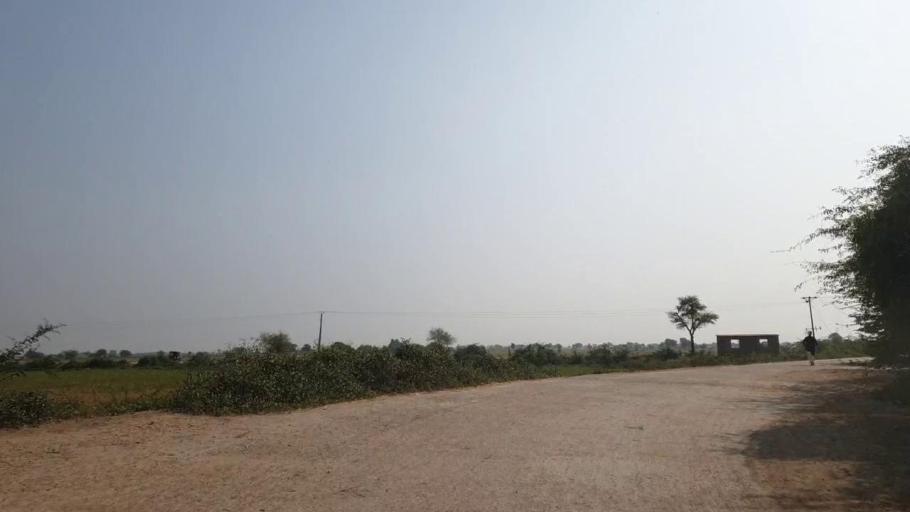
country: PK
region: Sindh
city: Matli
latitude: 24.9627
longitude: 68.5843
